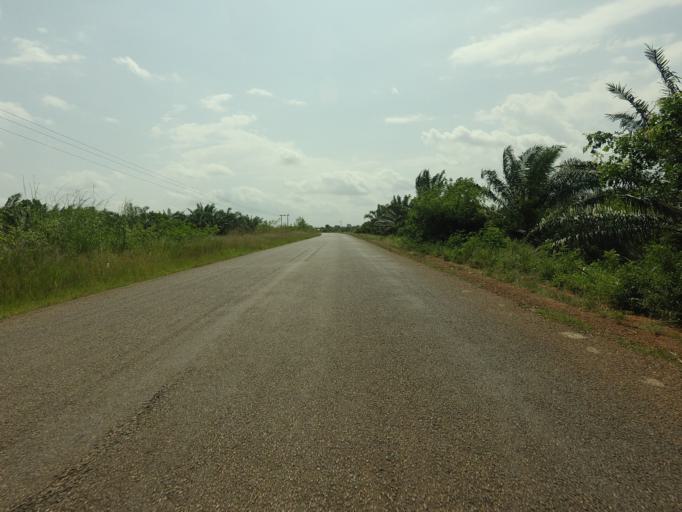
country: TG
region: Maritime
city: Lome
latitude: 6.2459
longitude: 0.9799
